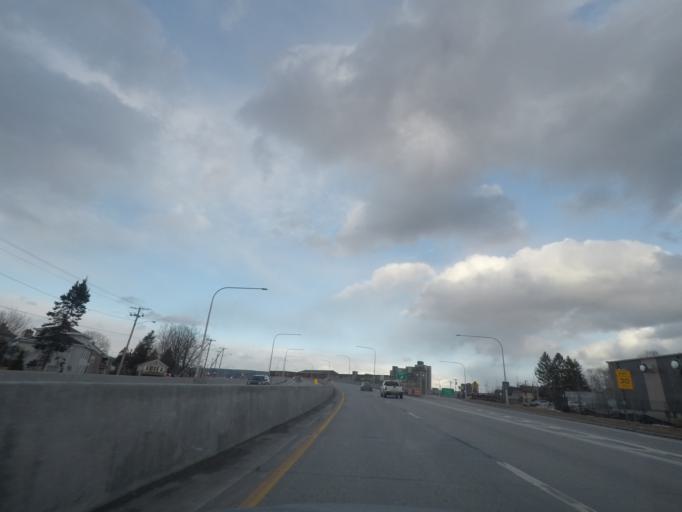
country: US
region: New York
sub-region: Oneida County
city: Utica
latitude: 43.1006
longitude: -75.2431
